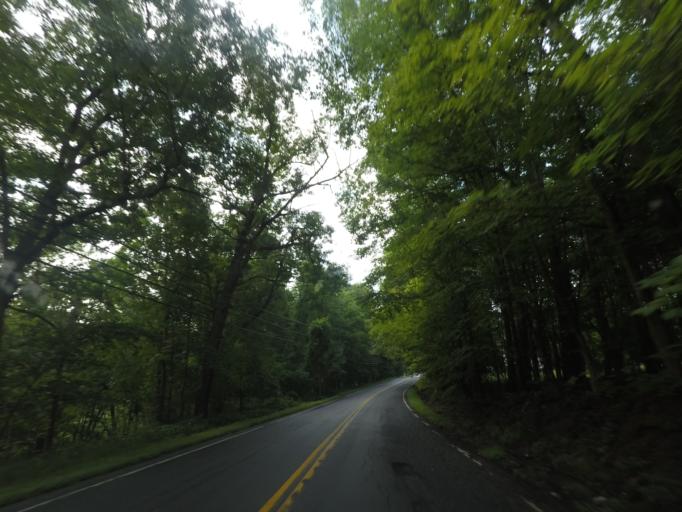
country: US
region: New York
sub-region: Rensselaer County
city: Nassau
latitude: 42.5236
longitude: -73.6081
